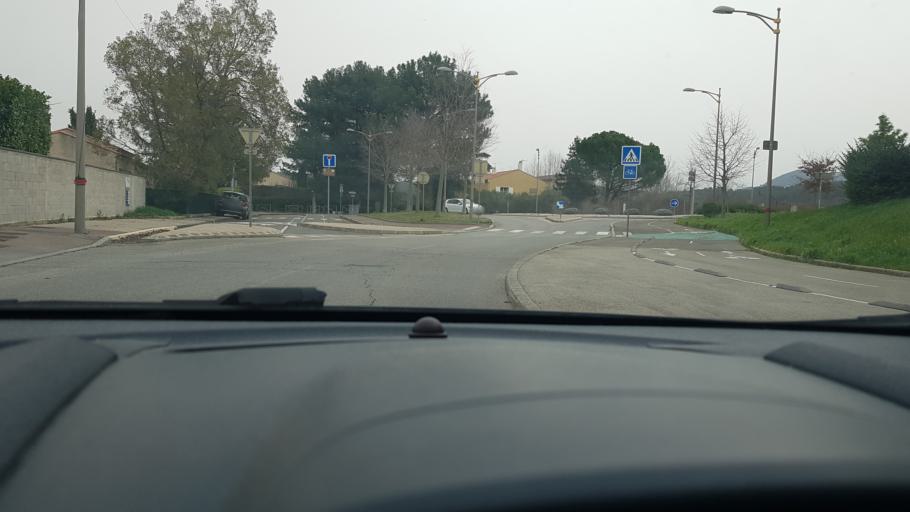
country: FR
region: Provence-Alpes-Cote d'Azur
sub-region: Departement des Bouches-du-Rhone
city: Gardanne
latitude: 43.4443
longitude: 5.4719
